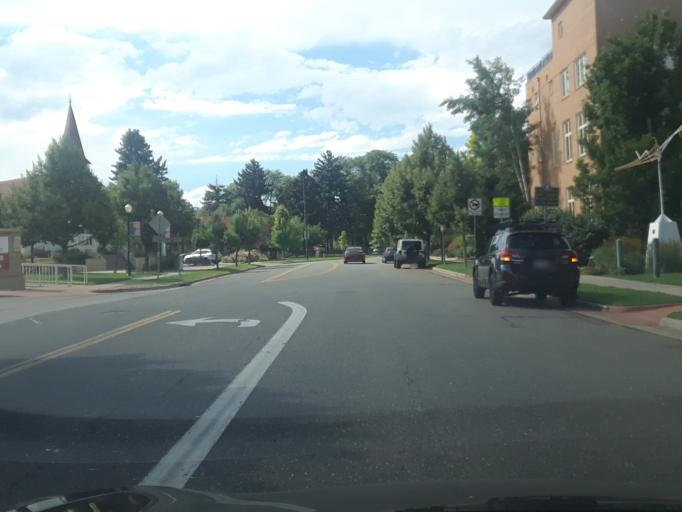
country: US
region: Colorado
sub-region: Arapahoe County
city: Glendale
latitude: 39.7208
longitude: -104.9007
